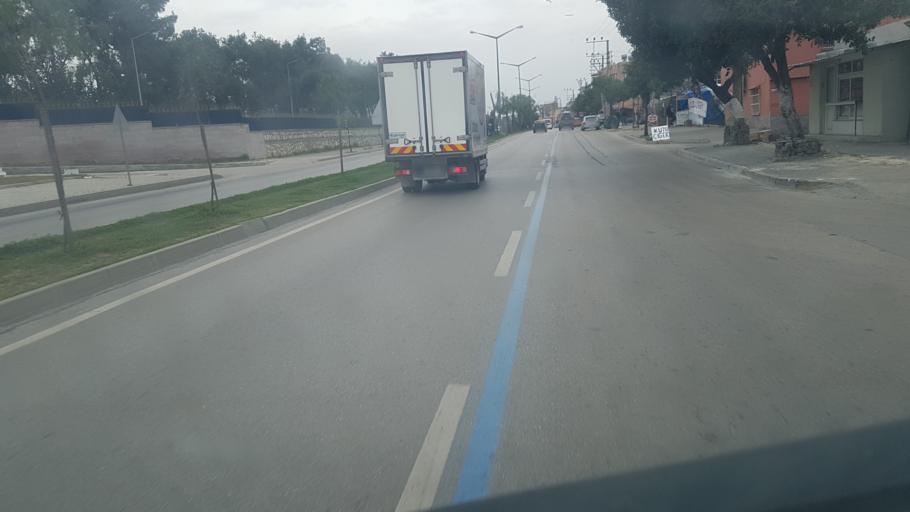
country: TR
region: Adana
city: Adana
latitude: 37.0196
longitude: 35.3416
